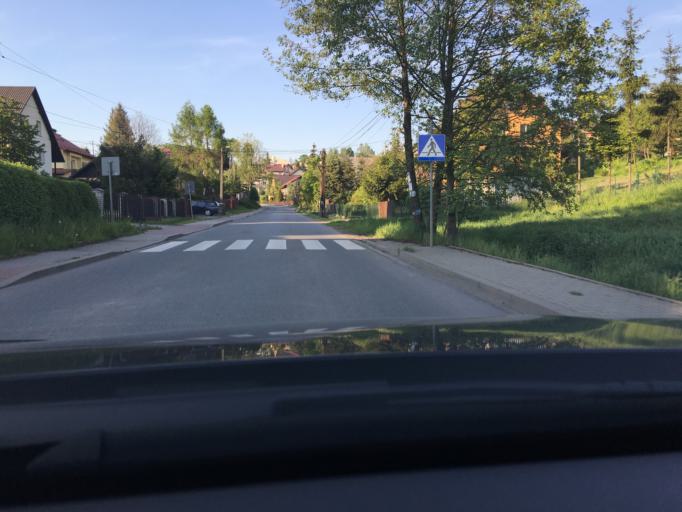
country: PL
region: Lesser Poland Voivodeship
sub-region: Powiat krakowski
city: Jerzmanowice
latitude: 50.2077
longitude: 19.7424
